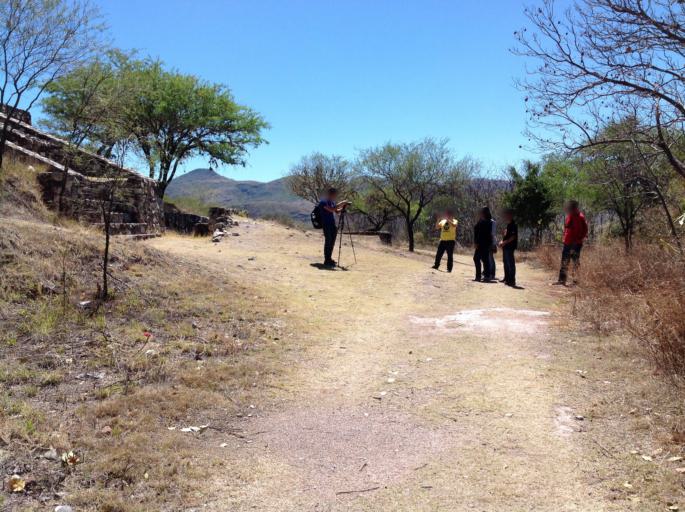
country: MX
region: Oaxaca
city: Ciudad de Huajuapam de Leon
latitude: 17.8174
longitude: -97.7737
